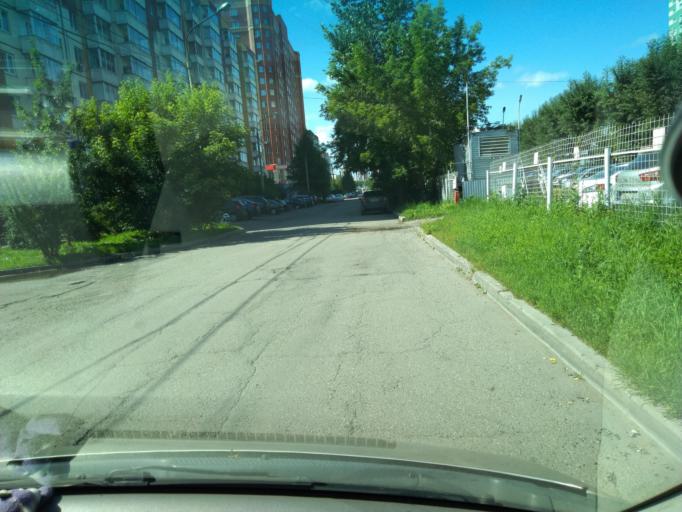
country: RU
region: Krasnoyarskiy
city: Krasnoyarsk
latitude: 56.0453
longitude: 92.9016
